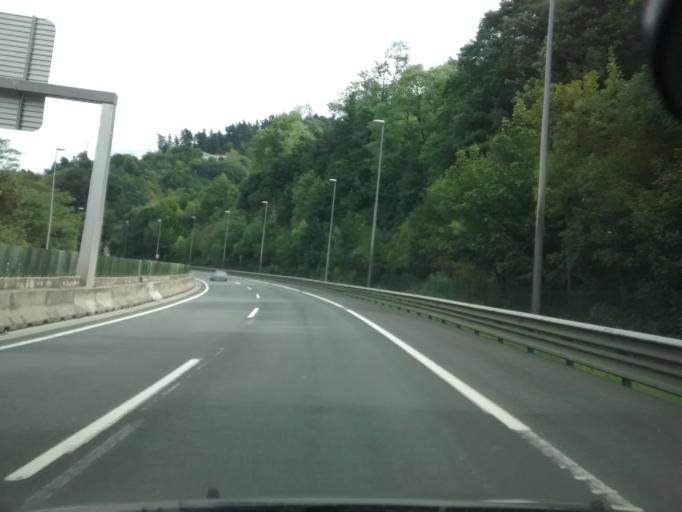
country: ES
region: Basque Country
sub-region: Bizkaia
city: Ermua
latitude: 43.1770
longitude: -2.4932
